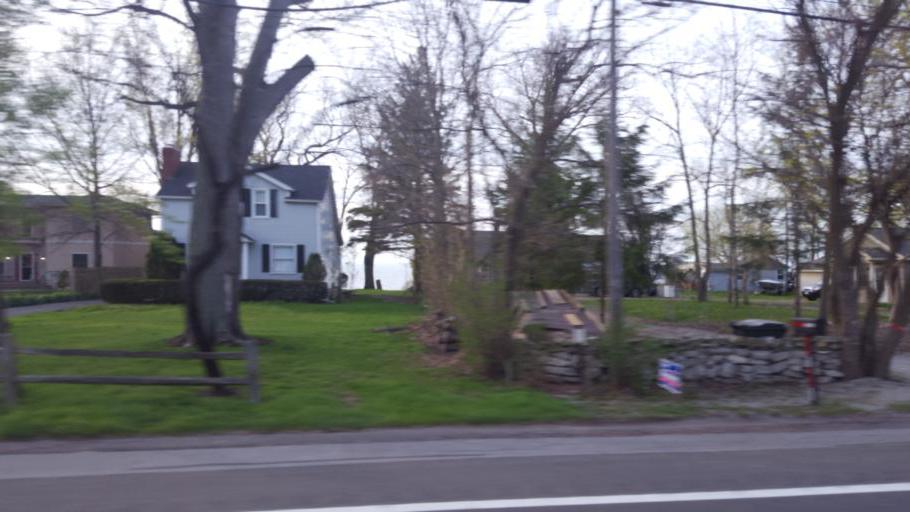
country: US
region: Ohio
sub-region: Lorain County
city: Vermilion
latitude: 41.4030
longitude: -82.4170
